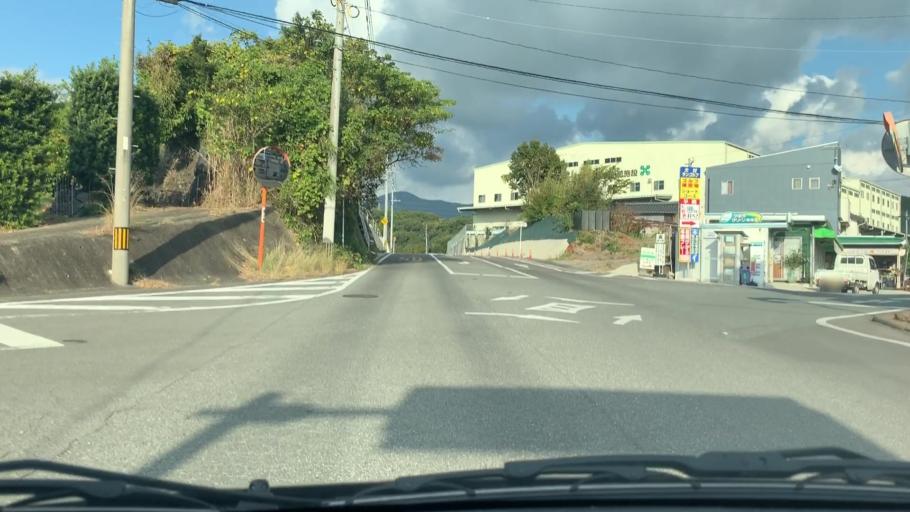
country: JP
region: Nagasaki
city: Omura
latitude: 32.9498
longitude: 129.9666
